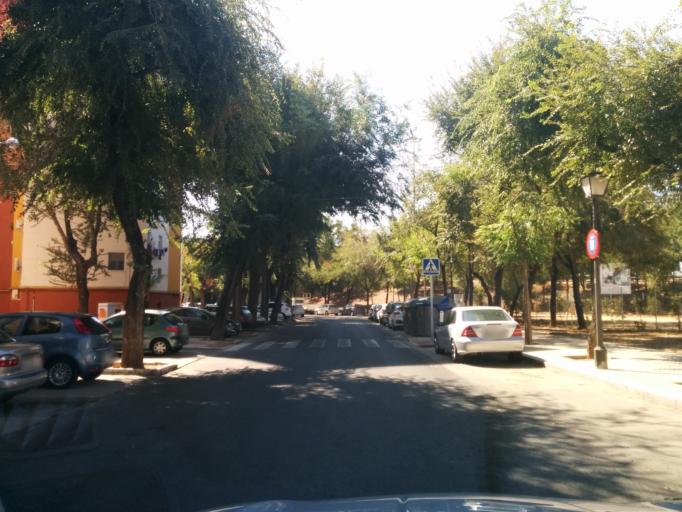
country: ES
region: Andalusia
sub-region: Provincia de Sevilla
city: San Juan de Aznalfarache
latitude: 37.3761
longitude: -6.0137
